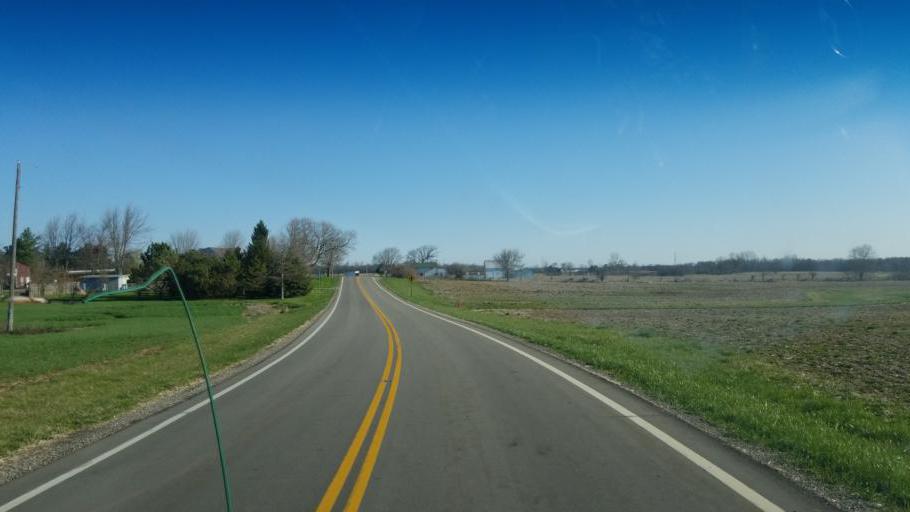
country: US
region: Ohio
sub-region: Logan County
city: Northwood
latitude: 40.5064
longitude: -83.6382
